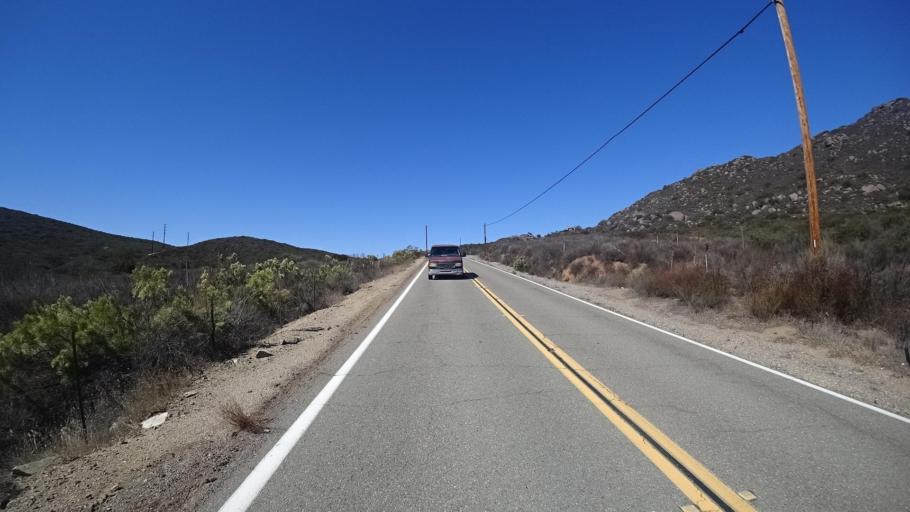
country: US
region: California
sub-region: San Diego County
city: Alpine
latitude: 32.8004
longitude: -116.7612
